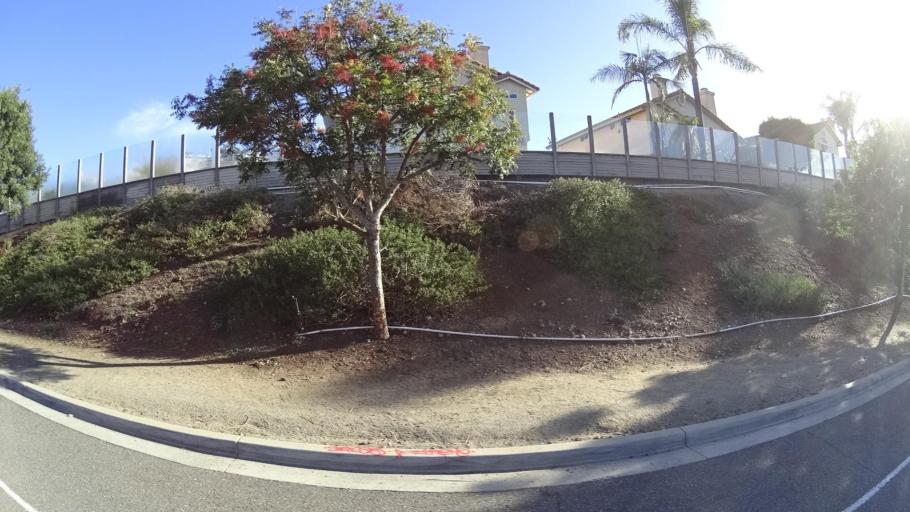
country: US
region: California
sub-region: San Diego County
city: La Presa
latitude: 32.7120
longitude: -116.9886
